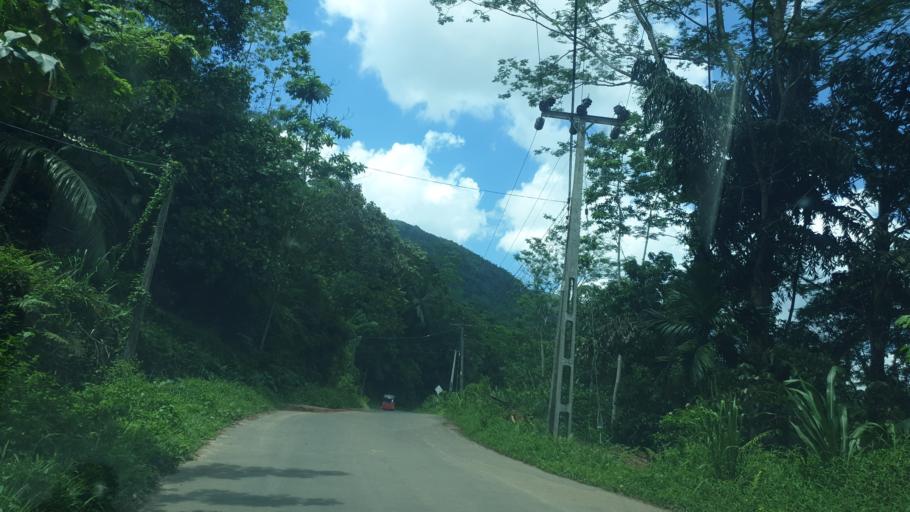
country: LK
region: Sabaragamuwa
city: Ratnapura
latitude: 6.4817
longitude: 80.4106
